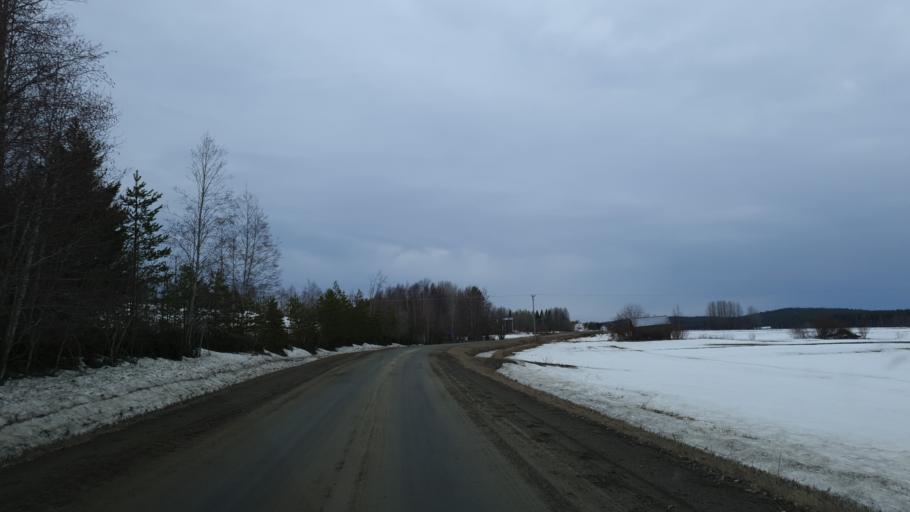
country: SE
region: Vaesterbotten
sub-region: Skelleftea Kommun
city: Burea
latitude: 64.3283
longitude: 21.1355
